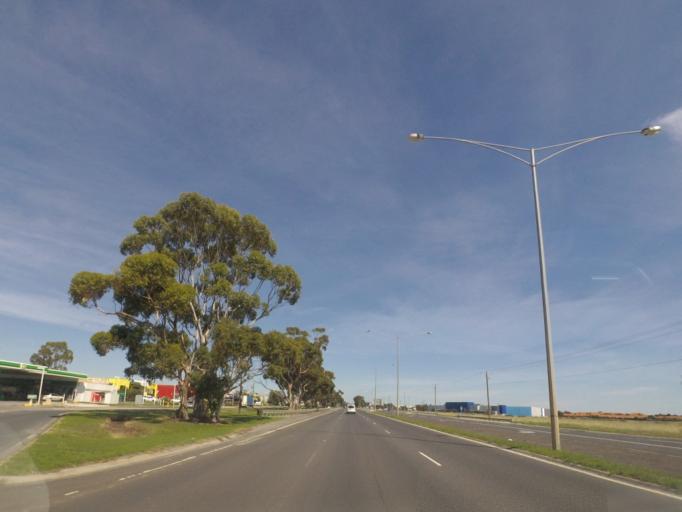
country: AU
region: Victoria
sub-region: Melton
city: Caroline Springs
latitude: -37.7619
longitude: 144.7536
